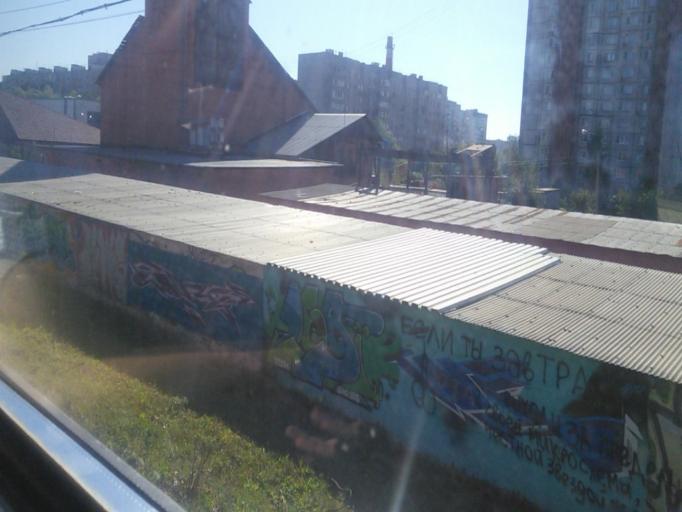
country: RU
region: Moskovskaya
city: Reutov
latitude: 55.7500
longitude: 37.8449
